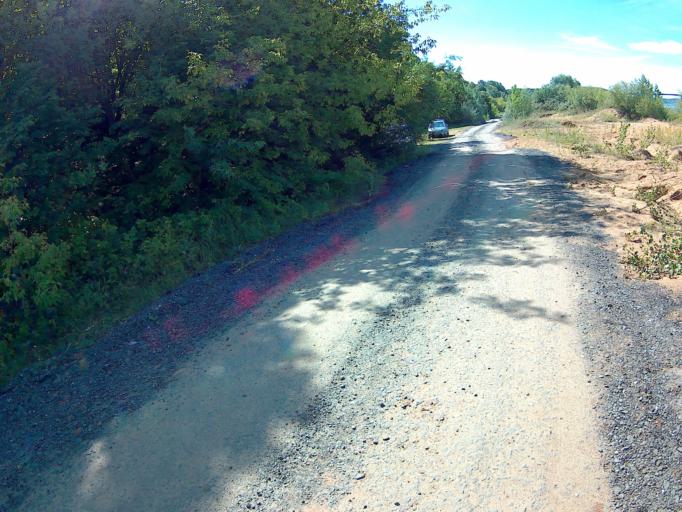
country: RU
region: Nizjnij Novgorod
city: Nizhniy Novgorod
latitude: 56.2628
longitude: 43.9678
